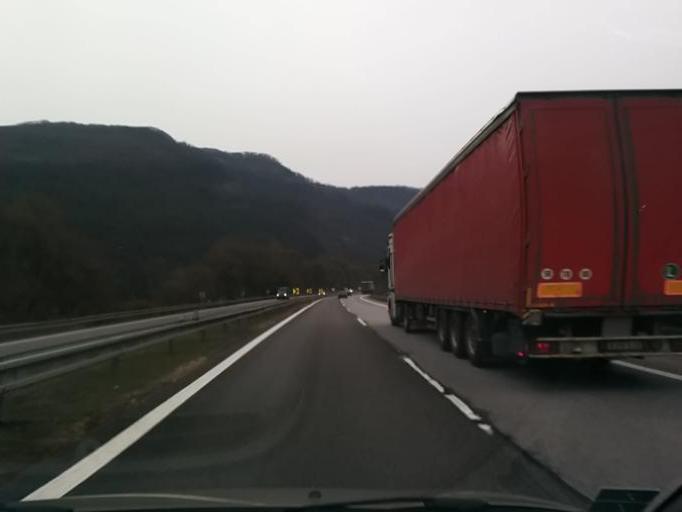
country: SK
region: Banskobystricky
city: Ziar nad Hronom
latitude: 48.5694
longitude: 18.9957
